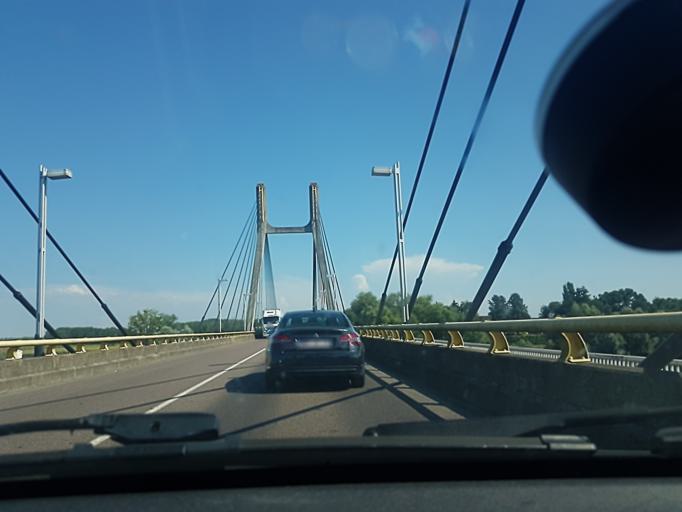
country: FR
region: Bourgogne
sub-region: Departement de Saone-et-Loire
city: Chalon-sur-Saone
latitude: 46.7848
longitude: 4.8696
